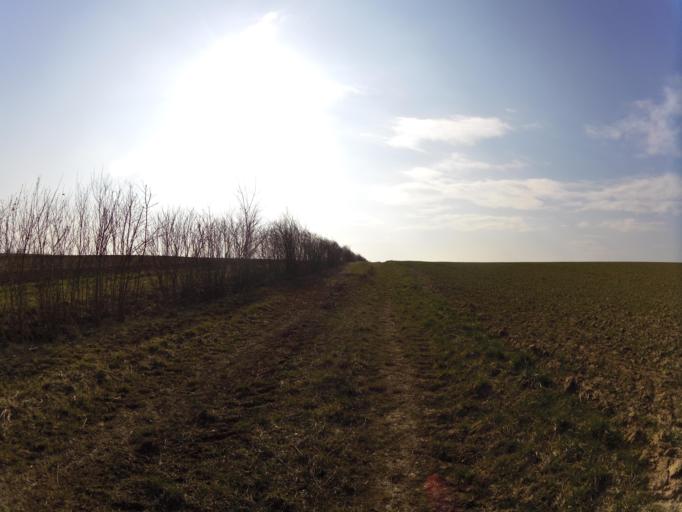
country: DE
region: Bavaria
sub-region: Regierungsbezirk Unterfranken
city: Sulzdorf
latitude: 49.6573
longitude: 9.9137
